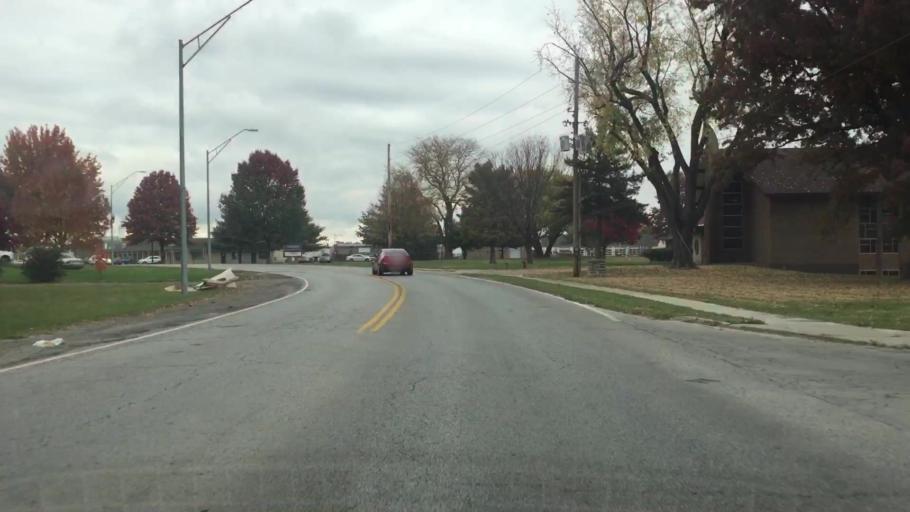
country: US
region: Missouri
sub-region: Jackson County
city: Raytown
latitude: 39.0415
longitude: -94.4370
